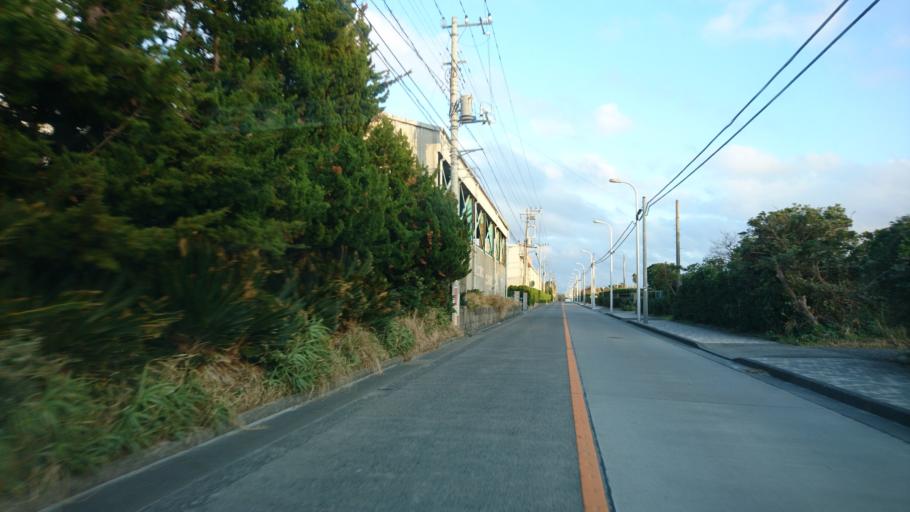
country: JP
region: Shizuoka
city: Shimoda
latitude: 34.3719
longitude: 139.2619
